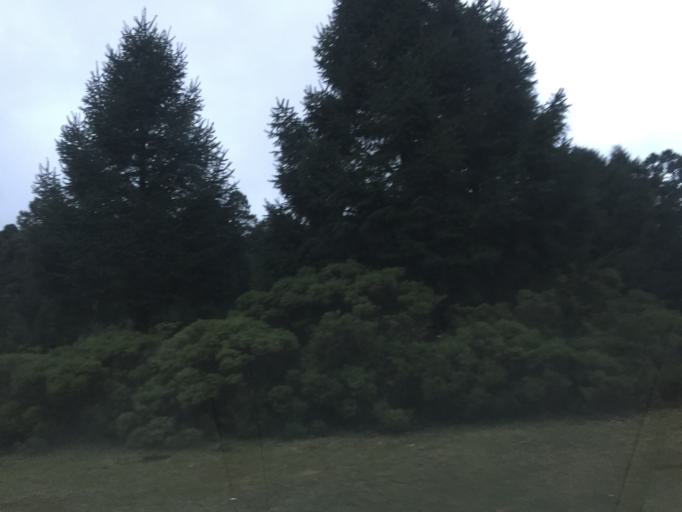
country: MX
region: Michoacan
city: Mineral de Angangueo
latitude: 19.6719
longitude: -100.2776
